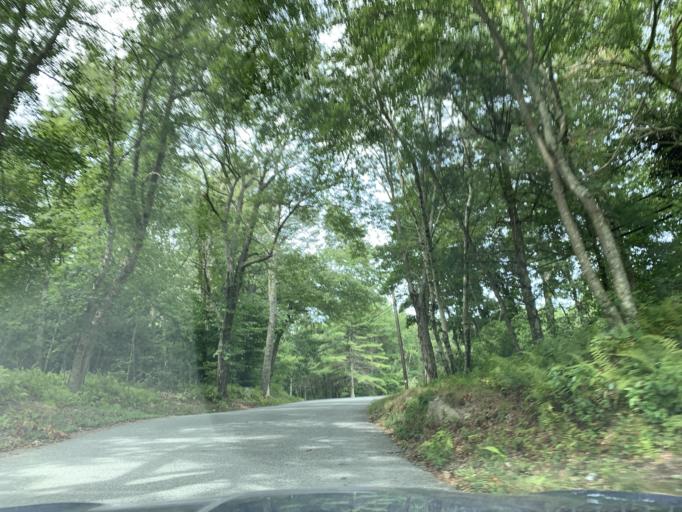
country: US
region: Rhode Island
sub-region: Kent County
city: West Greenwich
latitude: 41.5787
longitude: -71.6182
